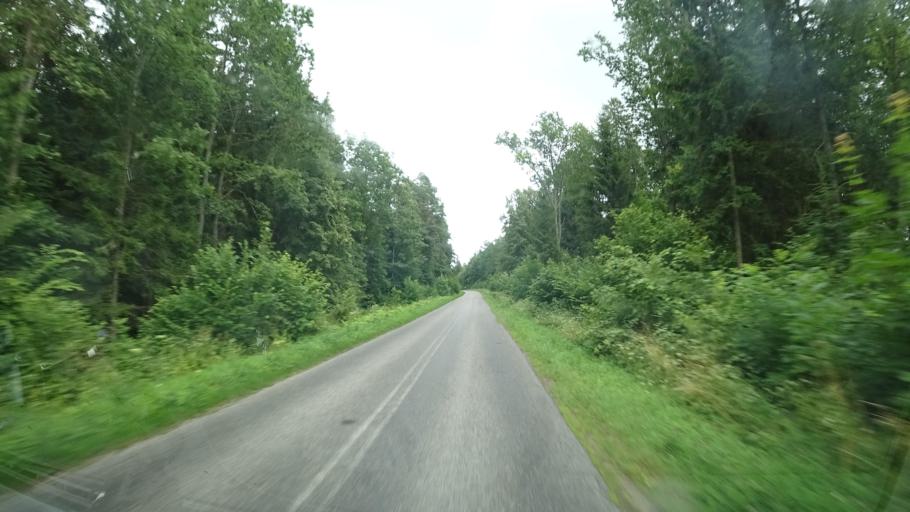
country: PL
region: Warmian-Masurian Voivodeship
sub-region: Powiat goldapski
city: Goldap
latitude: 54.3091
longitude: 22.3977
